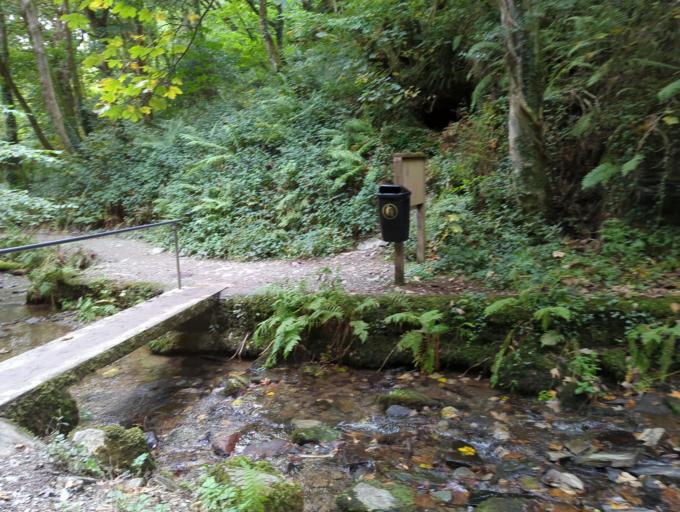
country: GB
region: England
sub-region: Cornwall
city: Tintagel
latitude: 50.6653
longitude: -4.7214
